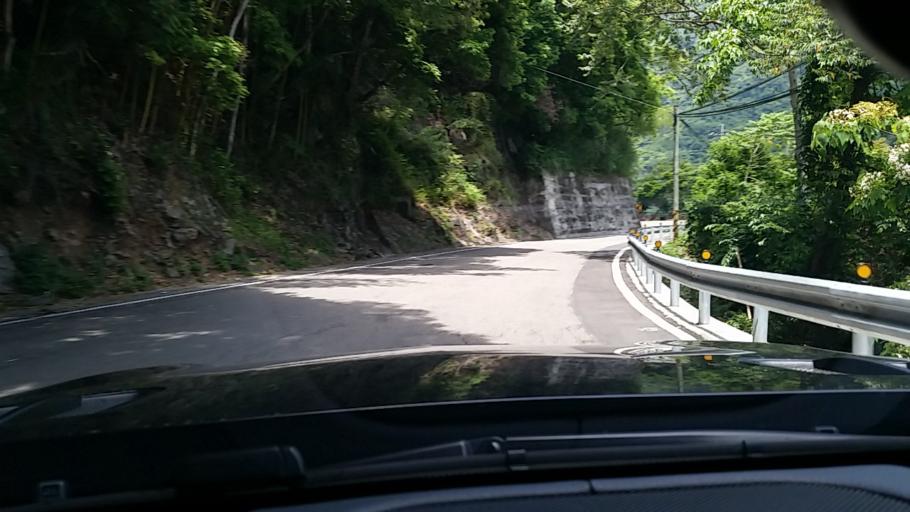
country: TW
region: Taiwan
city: Daxi
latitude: 24.7030
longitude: 121.3640
